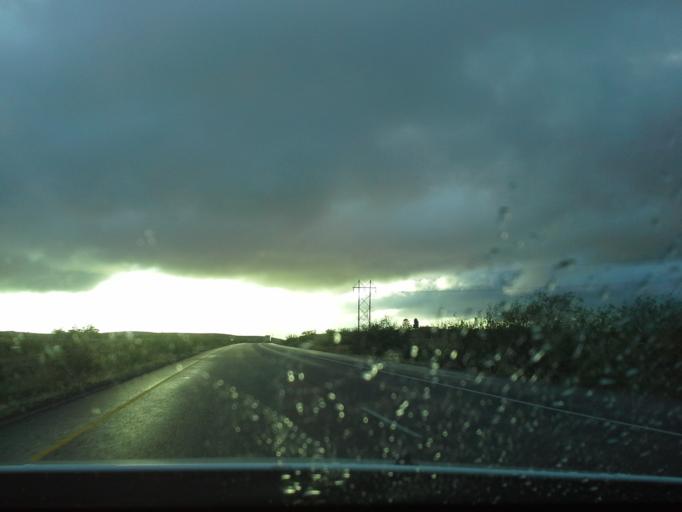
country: US
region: Arizona
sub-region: Cochise County
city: Mescal
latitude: 31.9637
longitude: -110.4528
